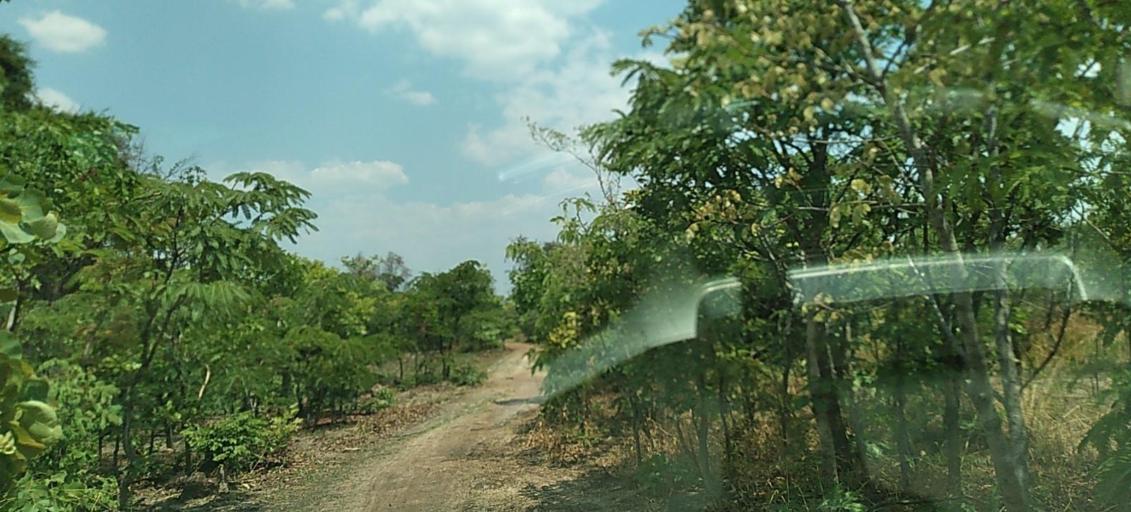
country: CD
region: Katanga
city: Kipushi
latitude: -12.0002
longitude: 27.4230
